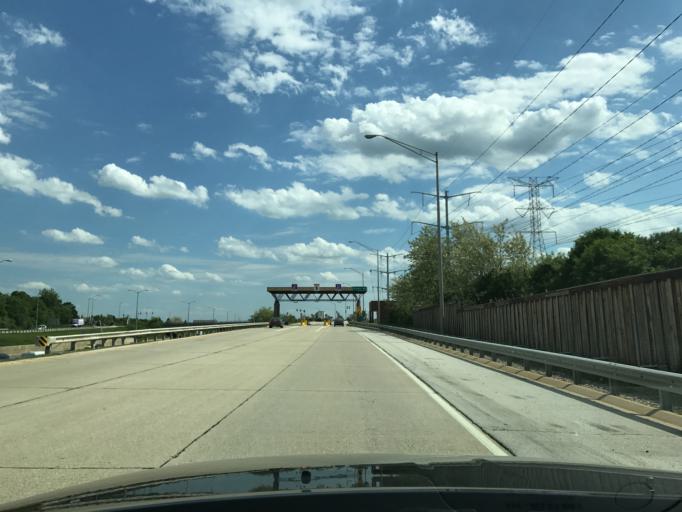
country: US
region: Illinois
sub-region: DuPage County
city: Lisle
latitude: 41.7888
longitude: -88.0570
